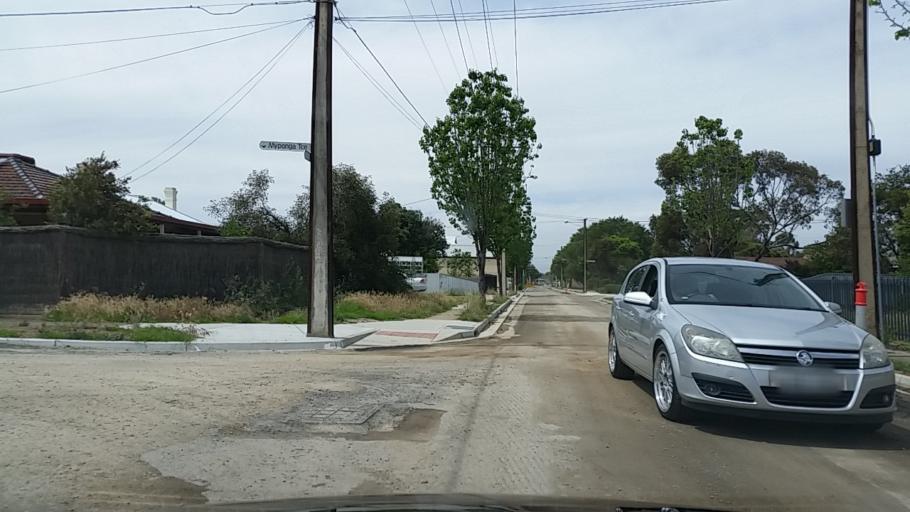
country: AU
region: South Australia
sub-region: Charles Sturt
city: Woodville
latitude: -34.8847
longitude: 138.5541
